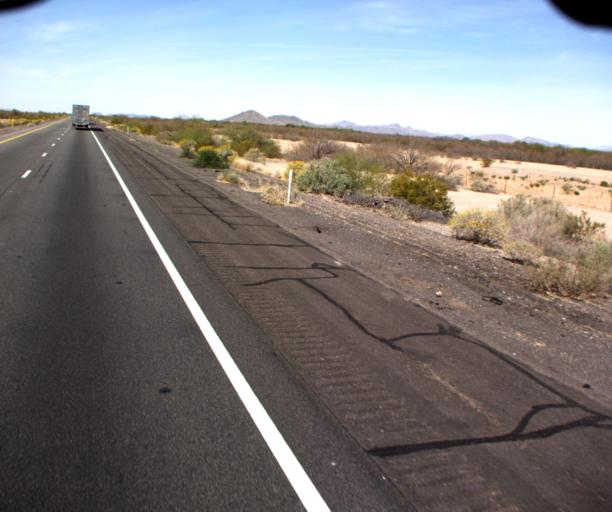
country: US
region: Arizona
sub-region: La Paz County
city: Salome
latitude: 33.5762
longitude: -113.3989
